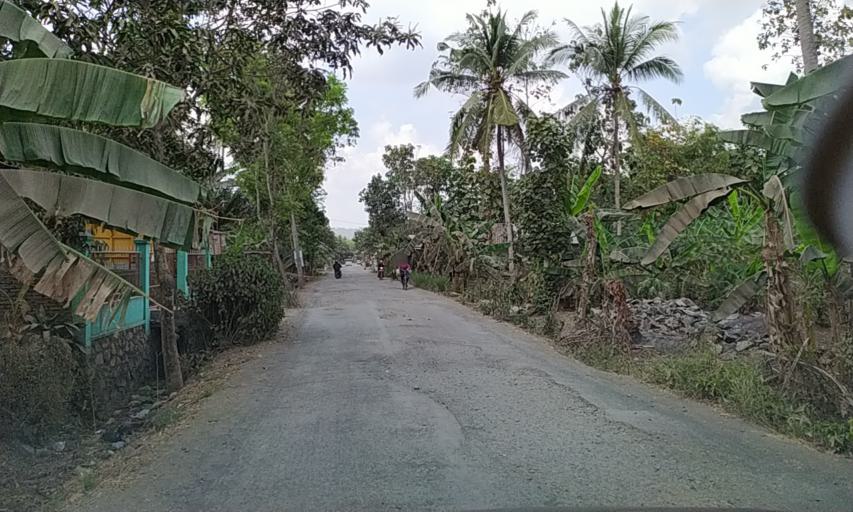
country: ID
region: Central Java
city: Cigintung
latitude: -7.3729
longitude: 108.8031
